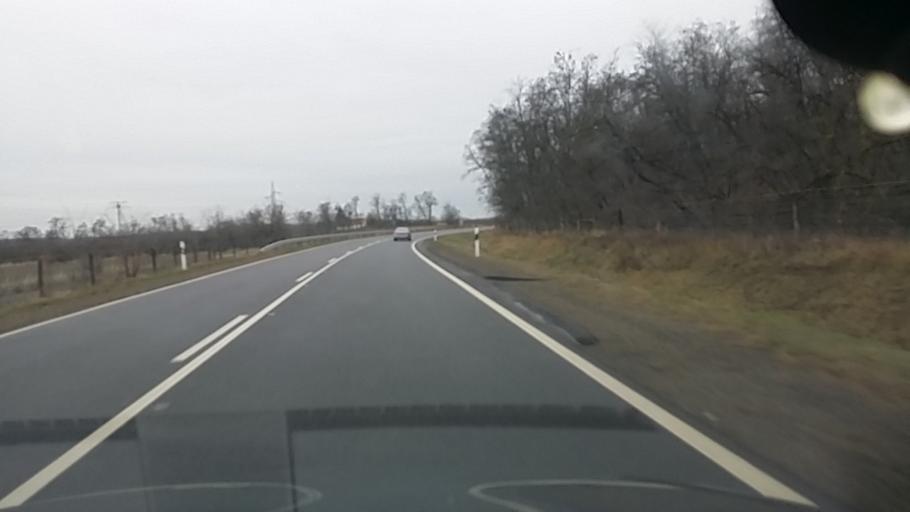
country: HU
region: Hajdu-Bihar
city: Debrecen
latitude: 47.6066
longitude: 21.6291
